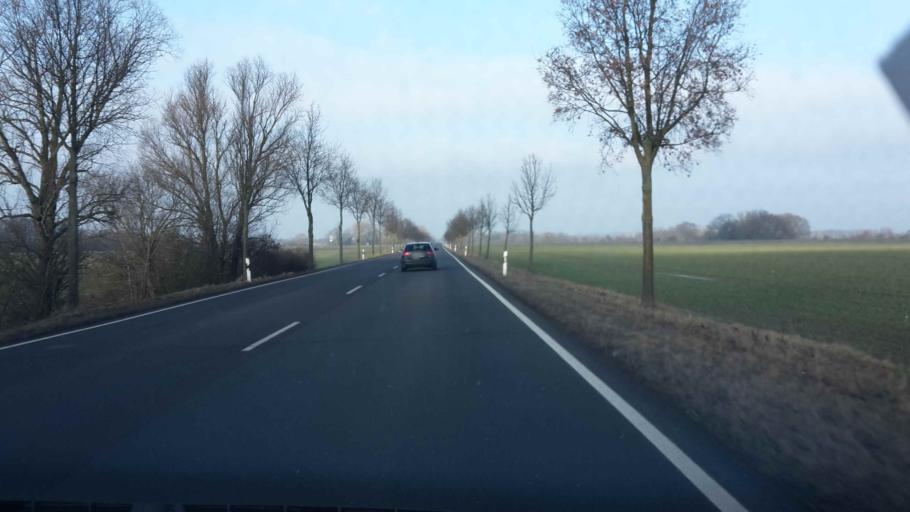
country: DE
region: Saxony-Anhalt
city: Seehausen
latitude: 52.9321
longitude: 11.7302
